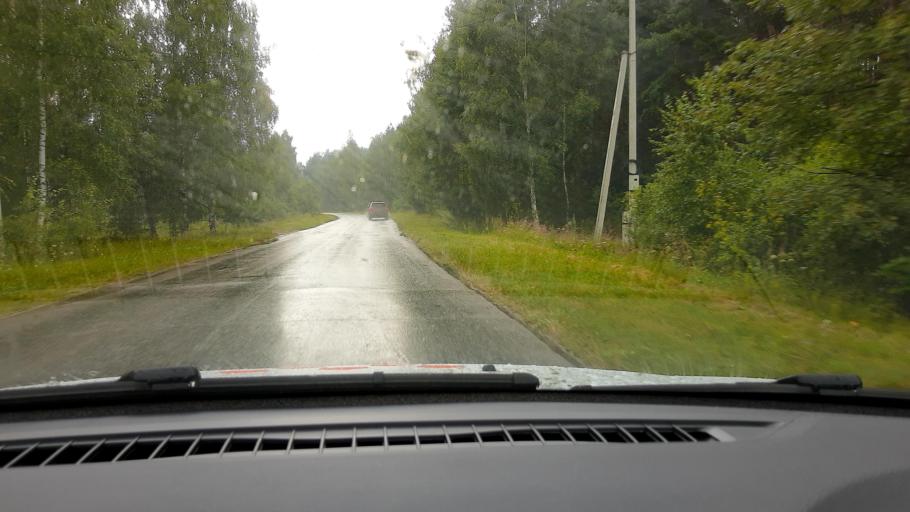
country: RU
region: Nizjnij Novgorod
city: Surovatikha
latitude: 55.9523
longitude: 43.9585
